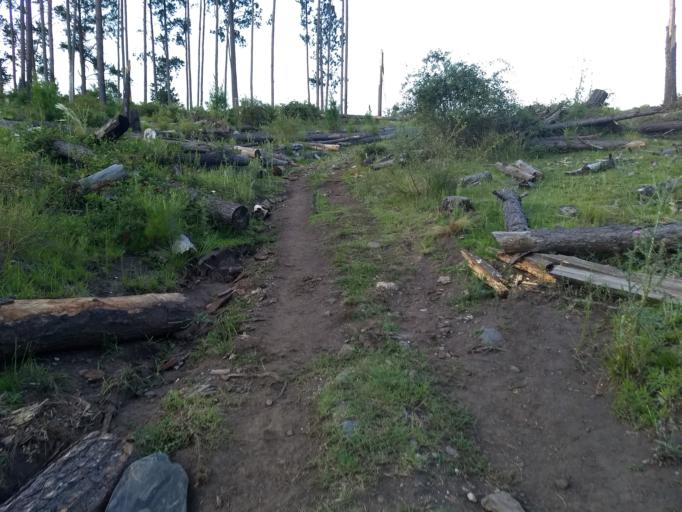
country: AR
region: Cordoba
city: Villa Berna
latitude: -31.9892
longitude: -64.8061
